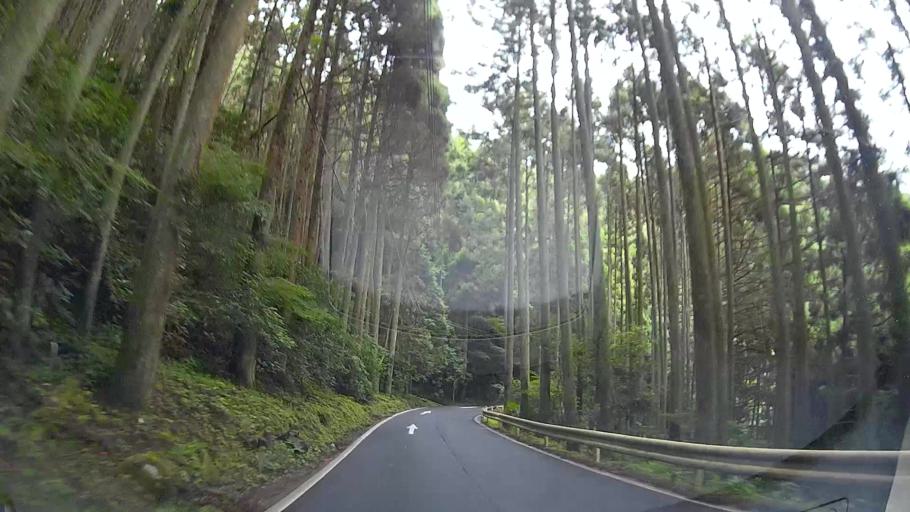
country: JP
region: Kumamoto
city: Kikuchi
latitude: 33.0997
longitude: 130.9590
